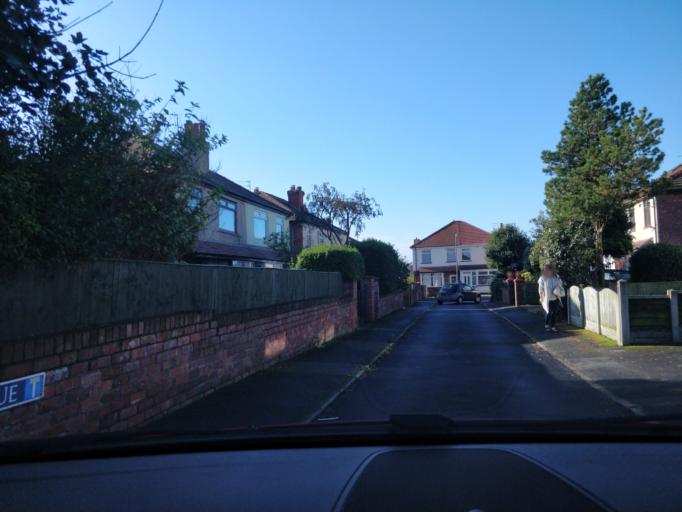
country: GB
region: England
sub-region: Sefton
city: Southport
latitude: 53.6328
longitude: -2.9975
